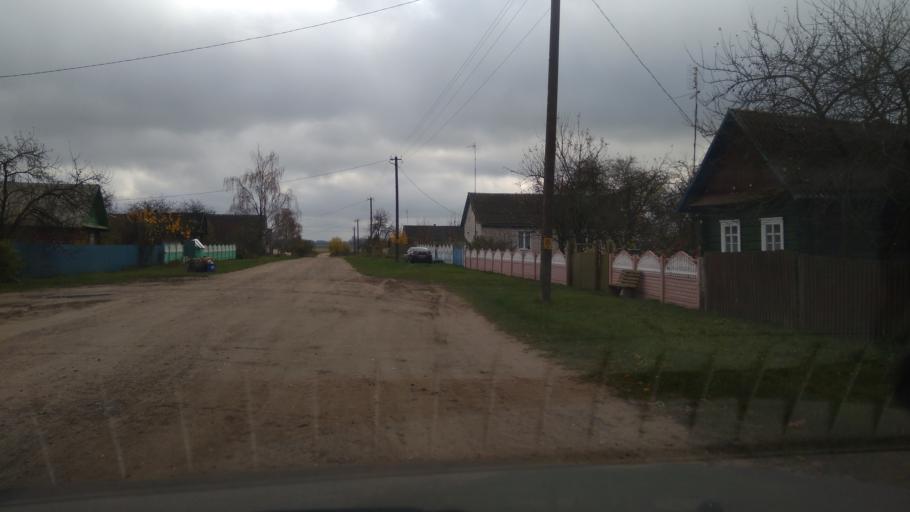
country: BY
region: Minsk
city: Staryya Darohi
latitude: 53.2031
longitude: 28.0440
